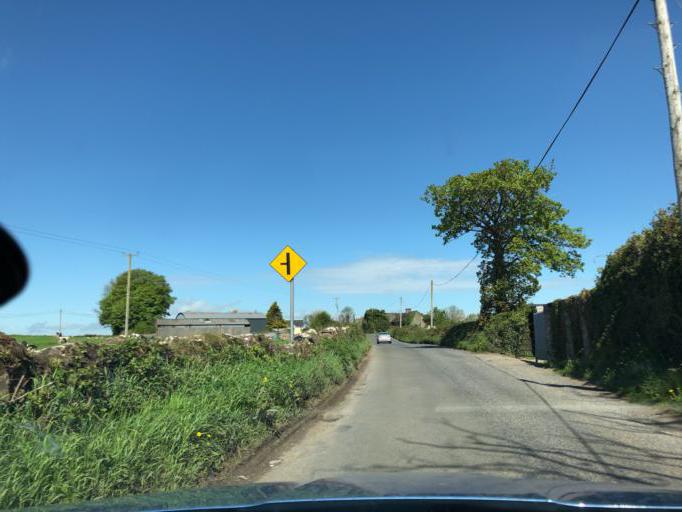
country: IE
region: Connaught
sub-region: County Galway
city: Portumna
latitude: 53.1558
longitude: -8.3863
